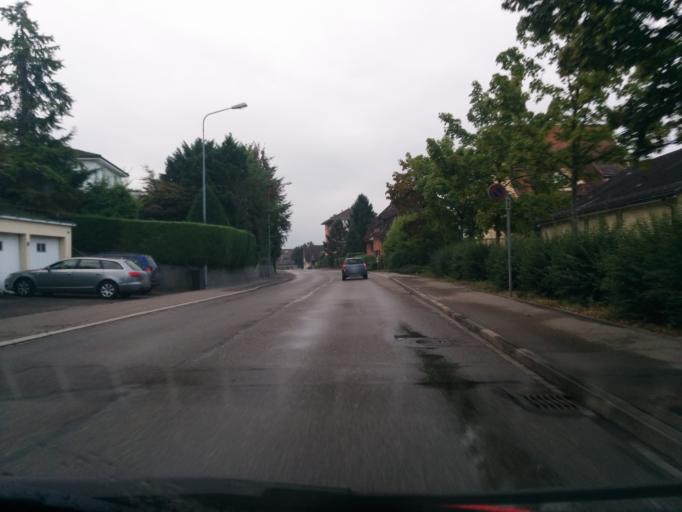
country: CH
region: Zurich
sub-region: Bezirk Meilen
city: Kuesnacht
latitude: 47.3219
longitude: 8.5830
